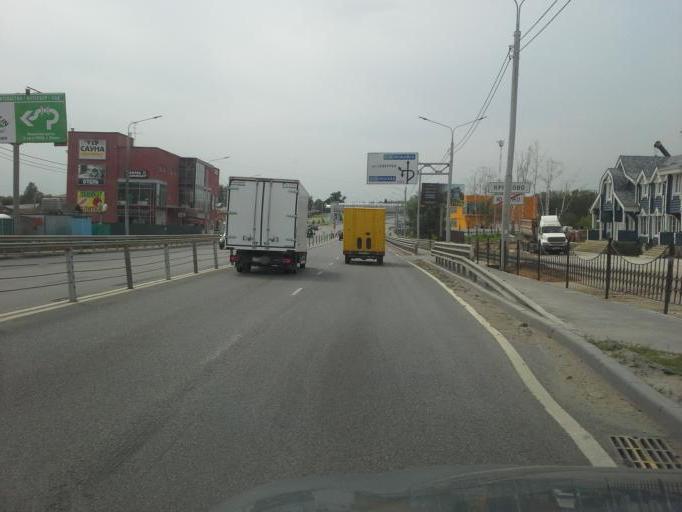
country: RU
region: Moskovskaya
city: Lesnoy Gorodok
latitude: 55.6578
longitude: 37.1814
